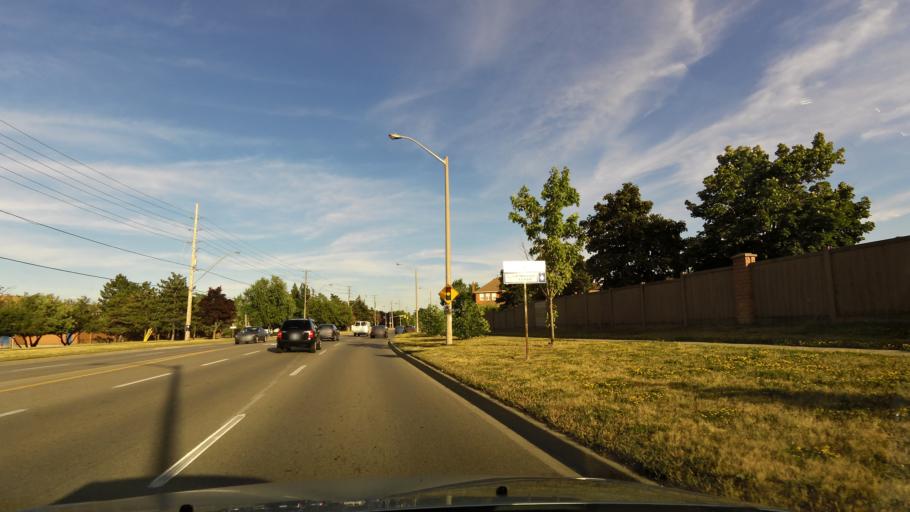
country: CA
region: Ontario
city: Brampton
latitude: 43.6741
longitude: -79.7201
